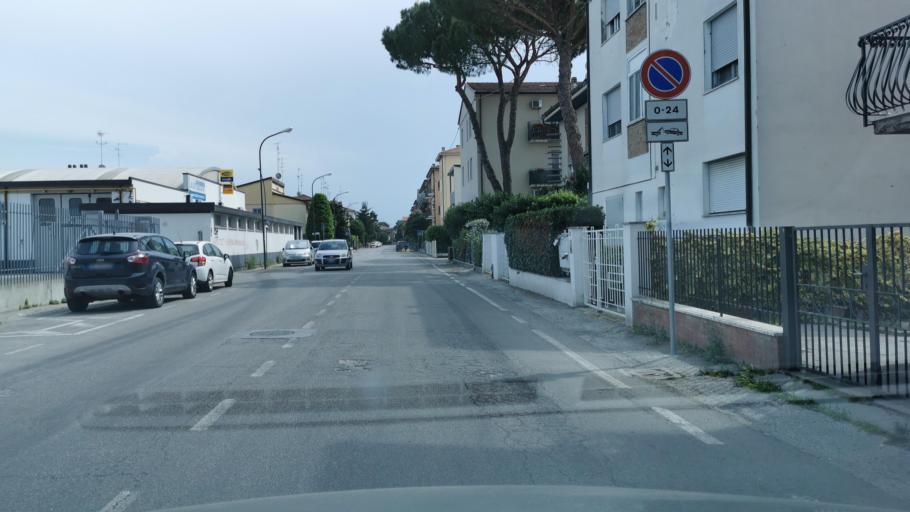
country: IT
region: Emilia-Romagna
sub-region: Provincia di Ravenna
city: Ravenna
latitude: 44.4218
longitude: 12.1809
